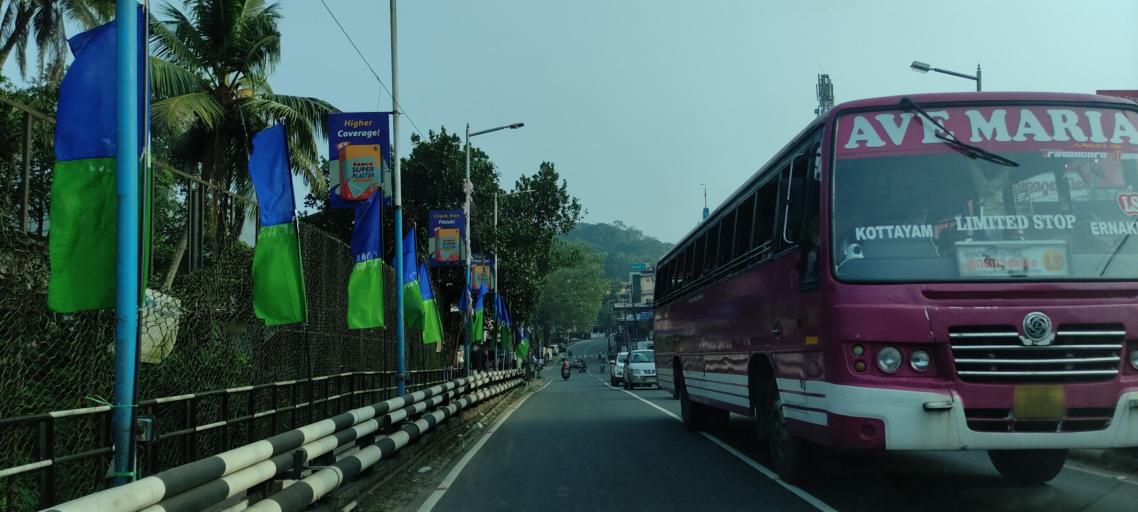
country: IN
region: Kerala
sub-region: Kottayam
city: Vaikam
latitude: 9.7661
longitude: 76.4919
